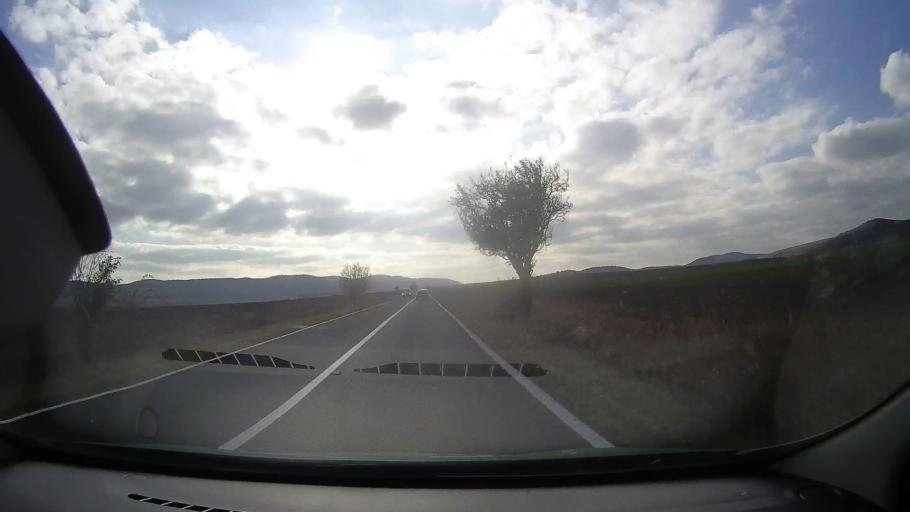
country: RO
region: Tulcea
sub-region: Comuna Nalbant
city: Nicolae Balcescu
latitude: 44.9841
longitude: 28.5528
